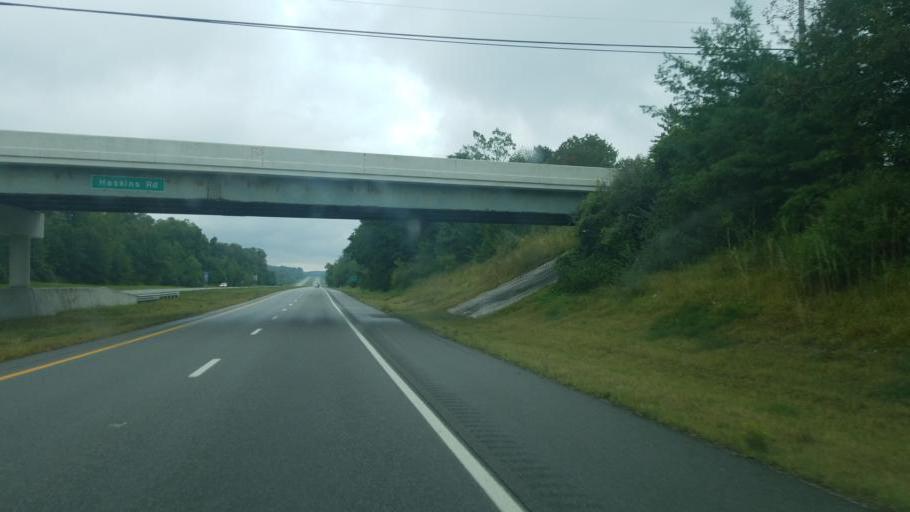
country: US
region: Ohio
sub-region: Geauga County
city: Bainbridge
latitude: 41.3856
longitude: -81.3236
